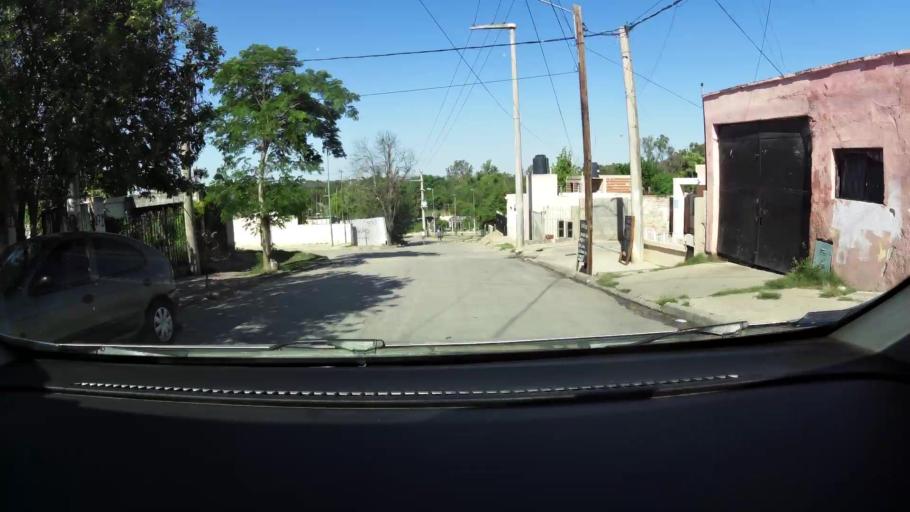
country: AR
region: Cordoba
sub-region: Departamento de Capital
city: Cordoba
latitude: -31.4051
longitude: -64.1507
